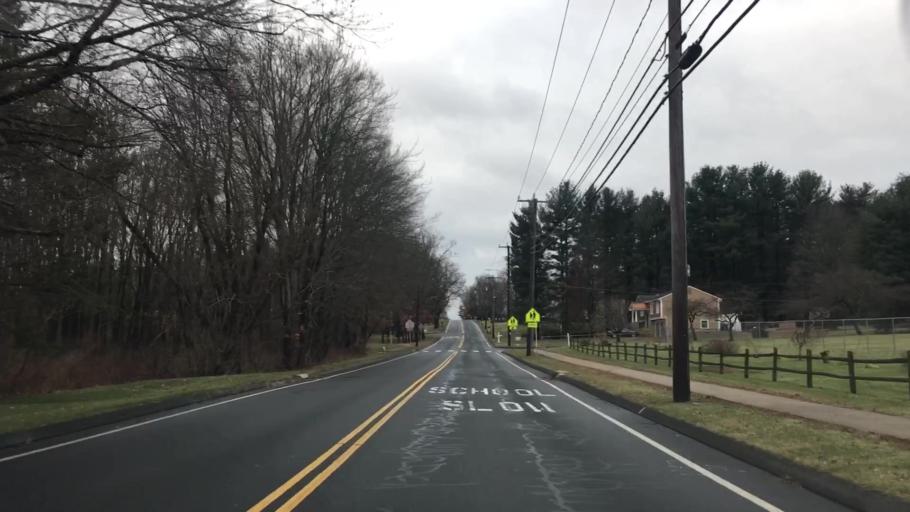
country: US
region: Connecticut
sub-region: Hartford County
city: Manchester
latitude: 41.8413
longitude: -72.5114
